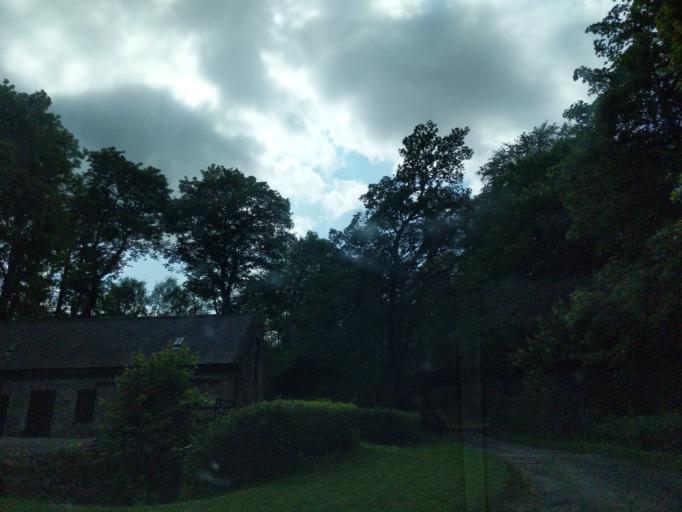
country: GB
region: Scotland
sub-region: Moray
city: Dufftown
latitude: 57.4670
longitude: -3.1344
